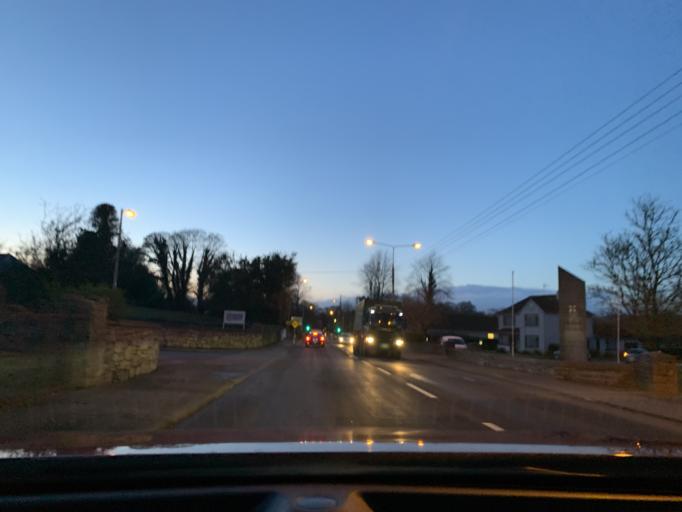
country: IE
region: Connaught
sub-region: Roscommon
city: Boyle
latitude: 53.9718
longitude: -8.2929
